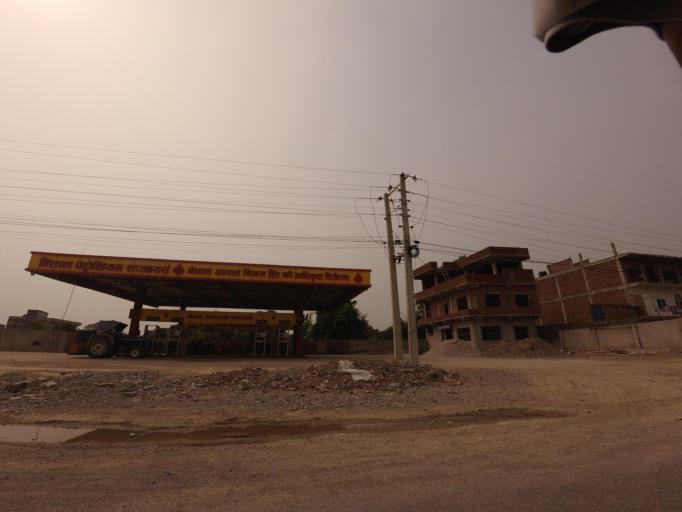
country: NP
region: Western Region
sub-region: Lumbini Zone
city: Bhairahawa
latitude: 27.5057
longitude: 83.3834
